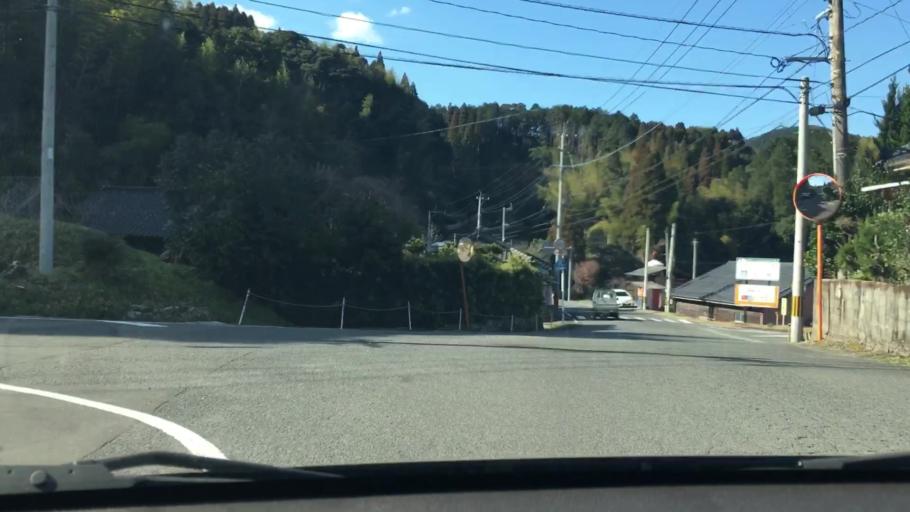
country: JP
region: Kagoshima
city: Ijuin
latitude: 31.7358
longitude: 130.4138
